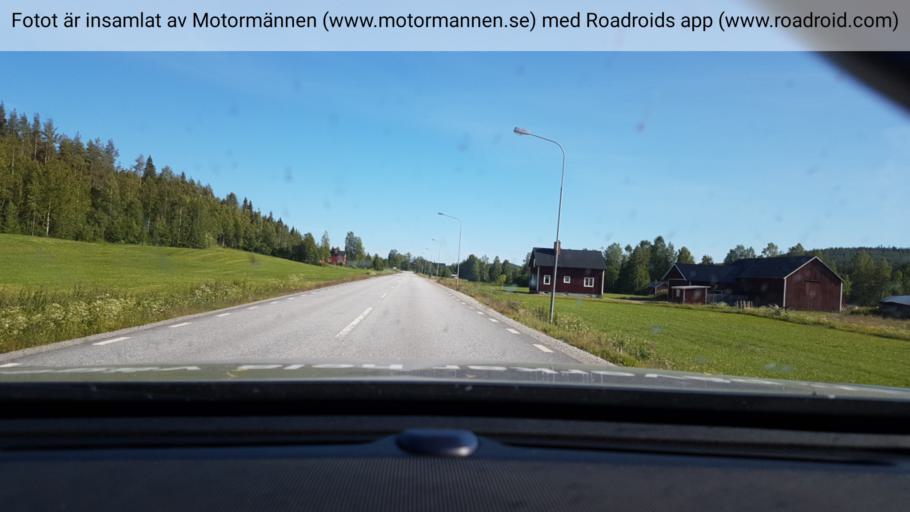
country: SE
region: Vaesterbotten
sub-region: Vindelns Kommun
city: Vindeln
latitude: 64.1448
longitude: 19.5172
